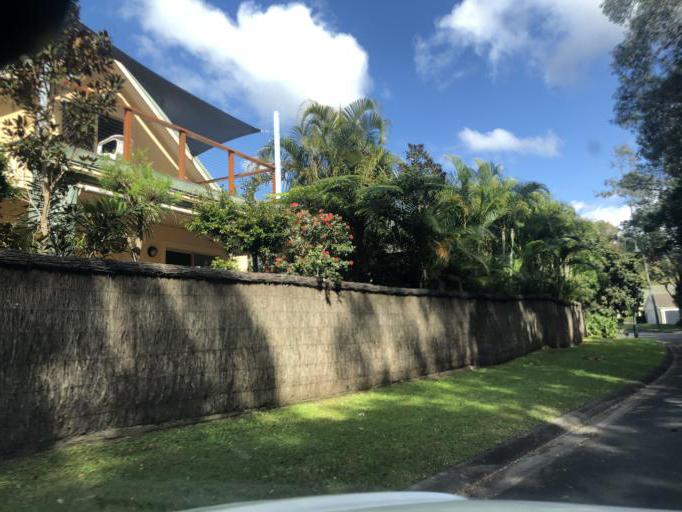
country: AU
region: New South Wales
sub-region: Coffs Harbour
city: Moonee Beach
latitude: -30.2299
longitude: 153.1517
